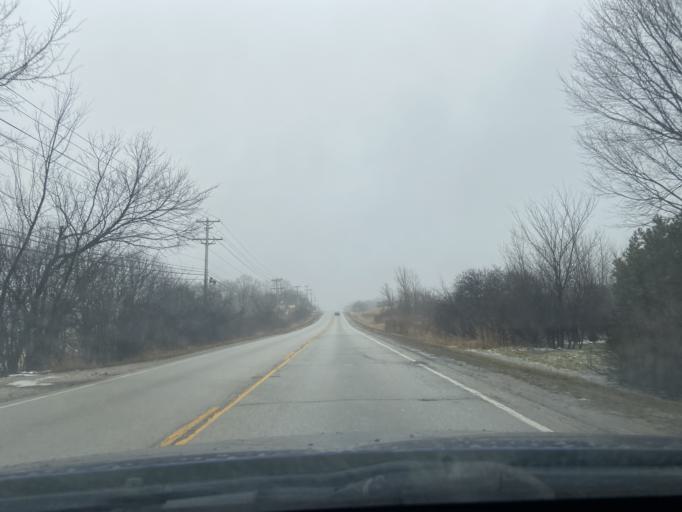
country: US
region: Illinois
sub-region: Lake County
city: Round Lake
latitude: 42.3148
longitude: -88.1066
